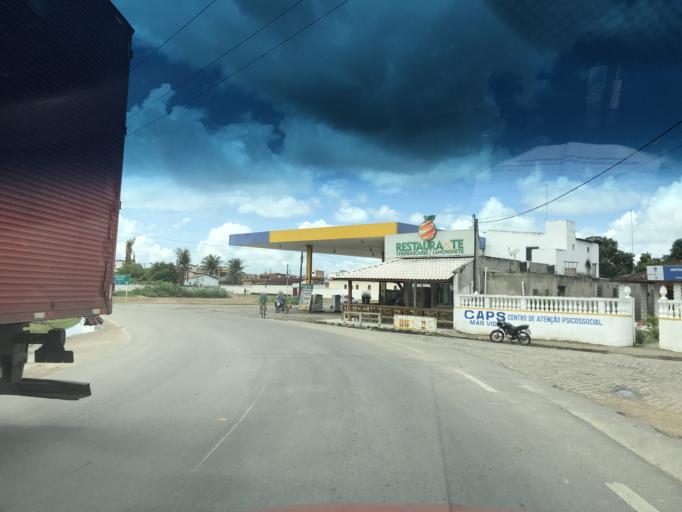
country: BR
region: Bahia
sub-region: Conceicao Do Almeida
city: Conceicao do Almeida
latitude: -12.7329
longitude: -39.1901
